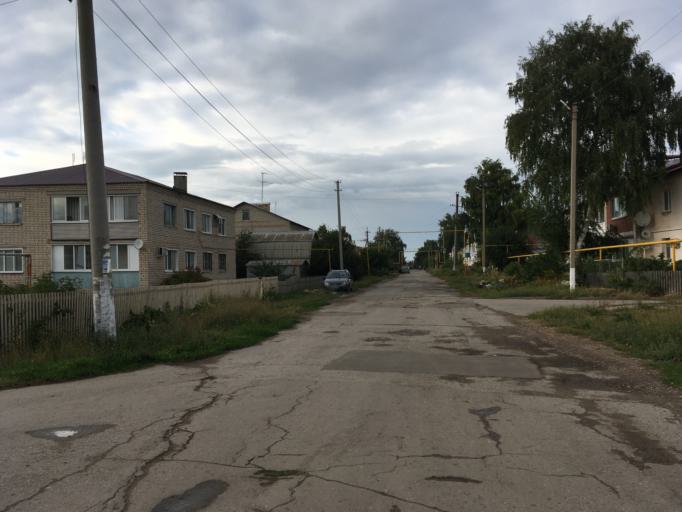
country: RU
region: Samara
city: Bezenchuk
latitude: 52.9862
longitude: 49.4443
